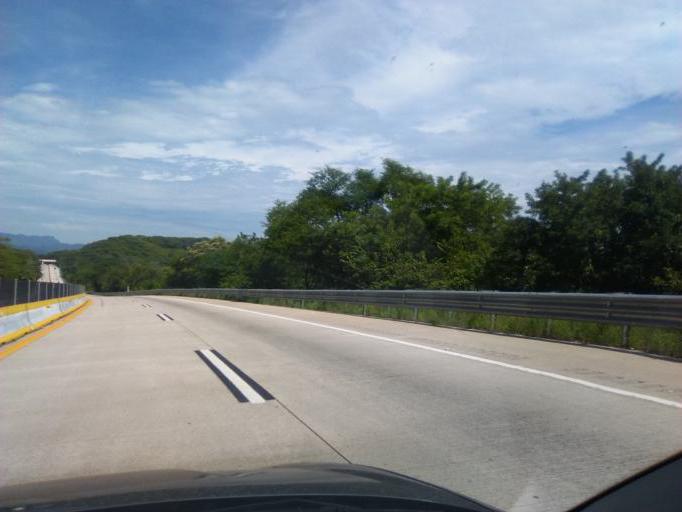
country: MX
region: Guerrero
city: Xaltianguis
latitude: 17.0048
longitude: -99.6696
